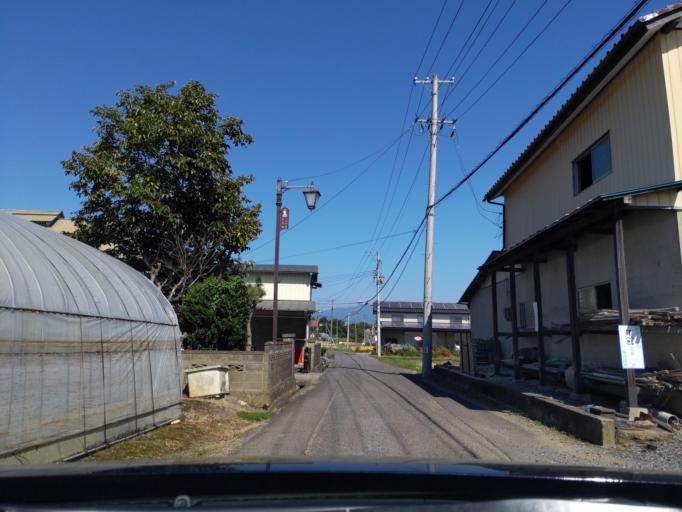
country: JP
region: Fukushima
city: Koriyama
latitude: 37.4224
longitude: 140.3074
